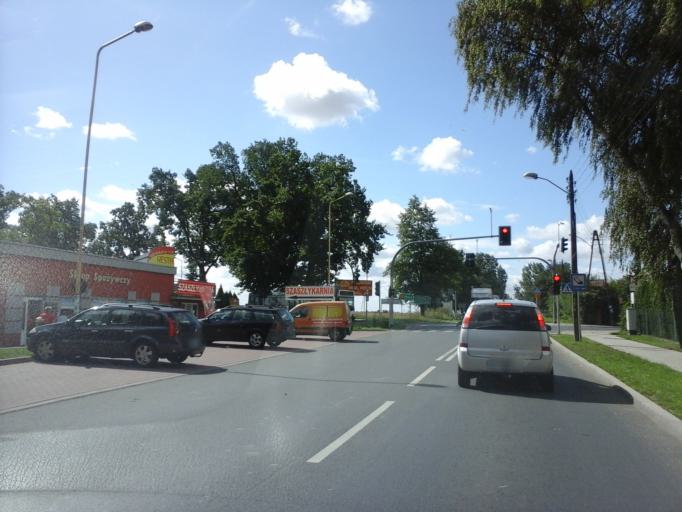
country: PL
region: West Pomeranian Voivodeship
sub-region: Powiat pyrzycki
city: Warnice
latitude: 53.2955
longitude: 15.0200
